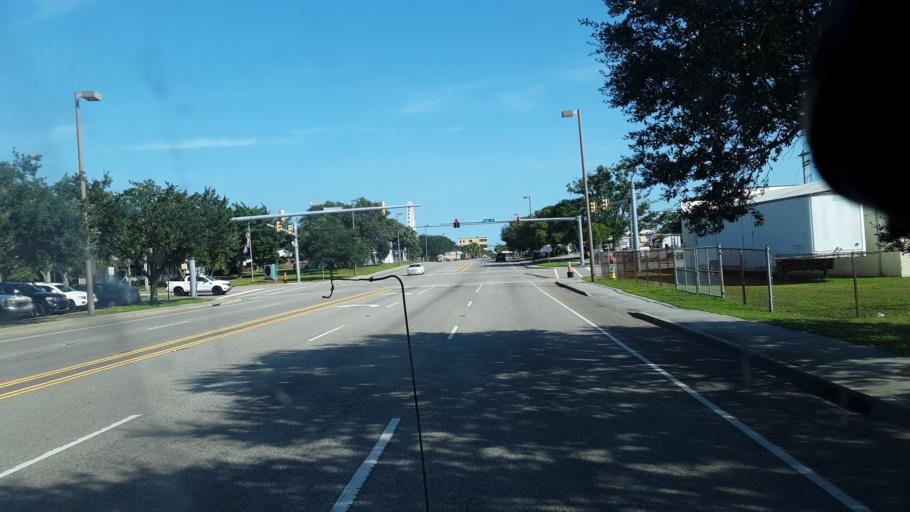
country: US
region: South Carolina
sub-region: Horry County
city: Myrtle Beach
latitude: 33.6974
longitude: -78.8827
